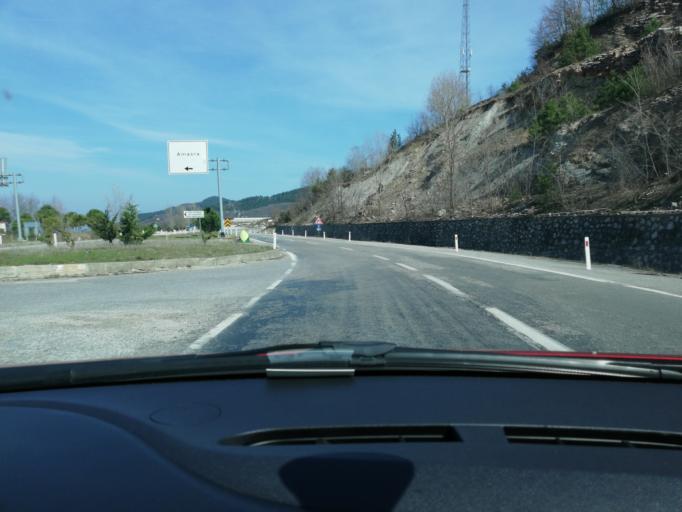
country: TR
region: Bartin
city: Amasra
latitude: 41.7381
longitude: 32.4281
